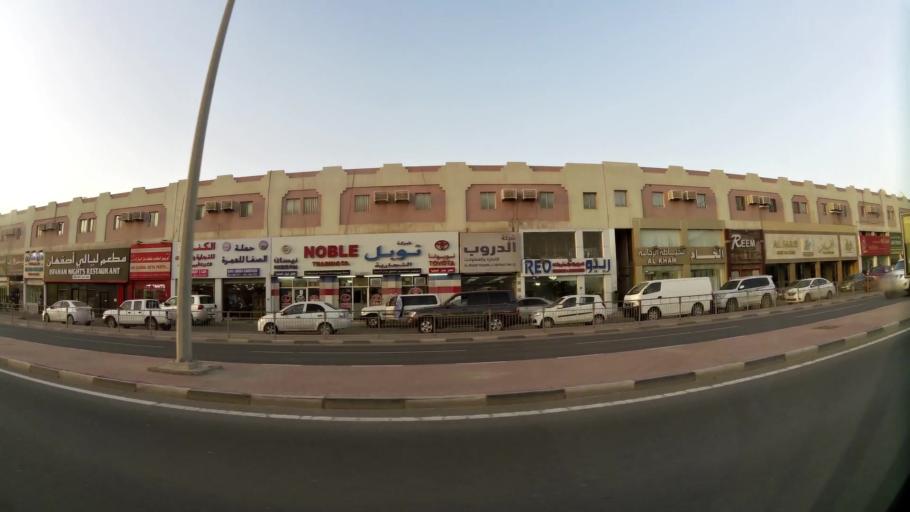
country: QA
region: Baladiyat ar Rayyan
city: Ar Rayyan
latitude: 25.3263
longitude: 51.4632
